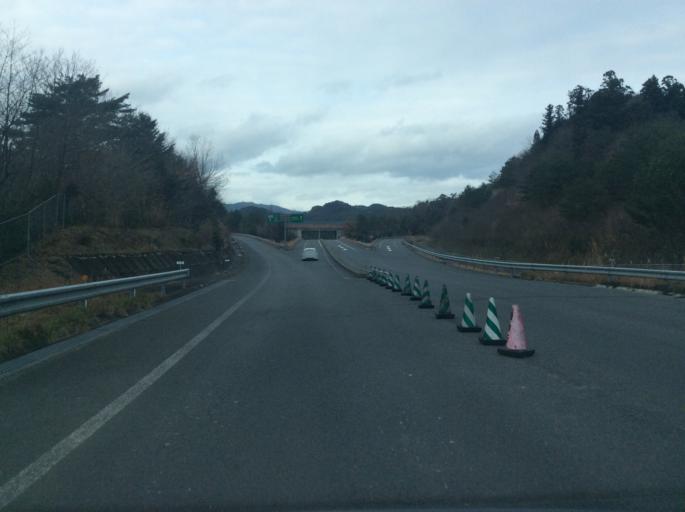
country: JP
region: Fukushima
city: Iwaki
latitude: 37.1247
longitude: 140.9475
